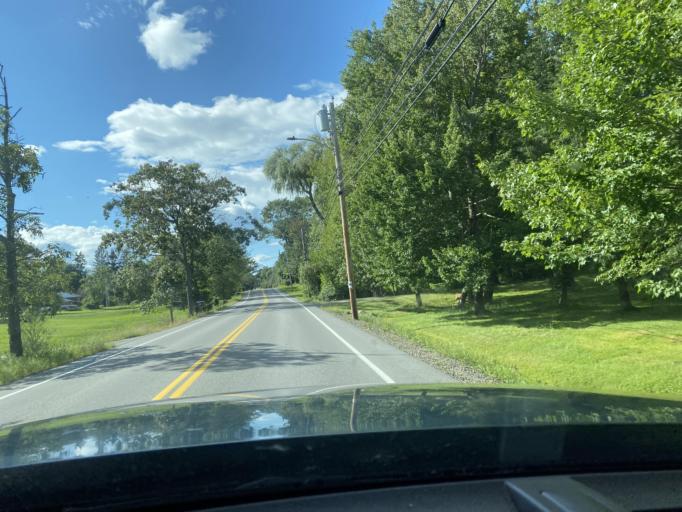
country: US
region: Maine
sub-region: York County
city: Kittery Point
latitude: 43.1438
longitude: -70.7063
